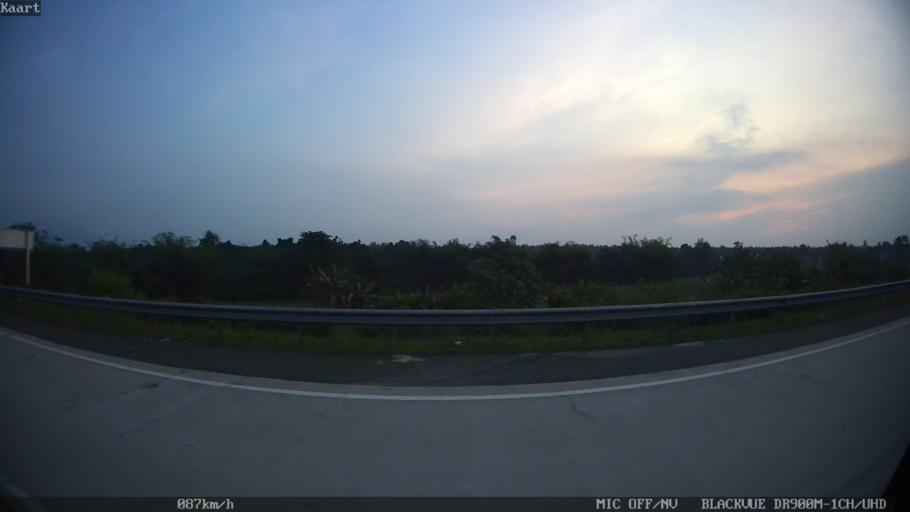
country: ID
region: Lampung
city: Kalianda
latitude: -5.6811
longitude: 105.6102
